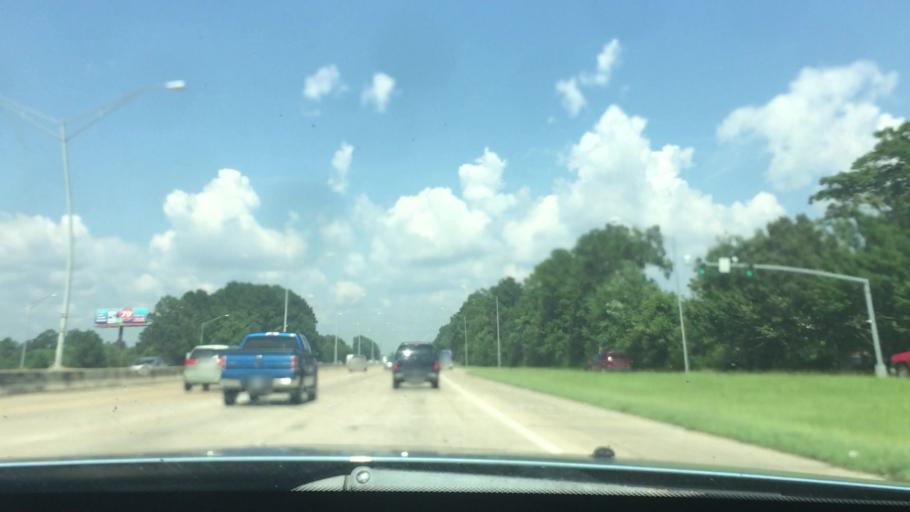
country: US
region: Louisiana
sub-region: East Baton Rouge Parish
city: Shenandoah
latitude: 30.4387
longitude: -91.0218
